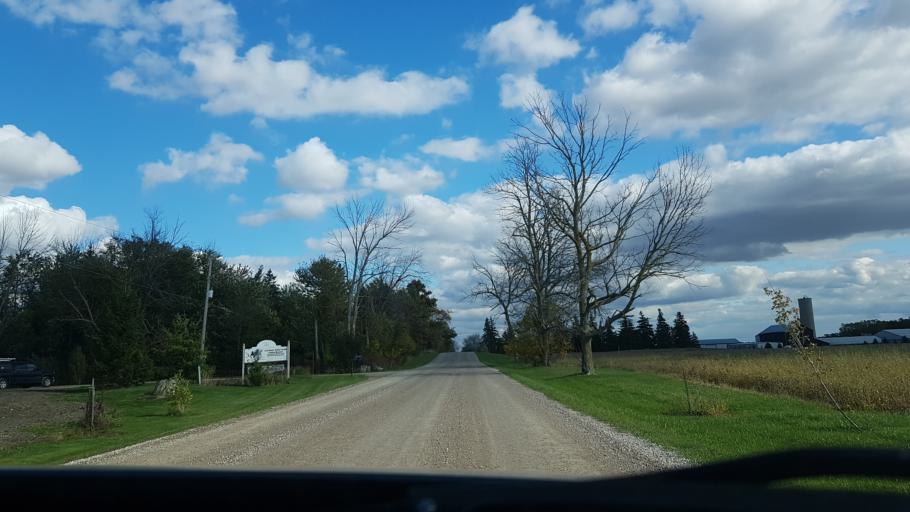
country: CA
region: Ontario
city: South Huron
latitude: 43.1113
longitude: -81.6395
